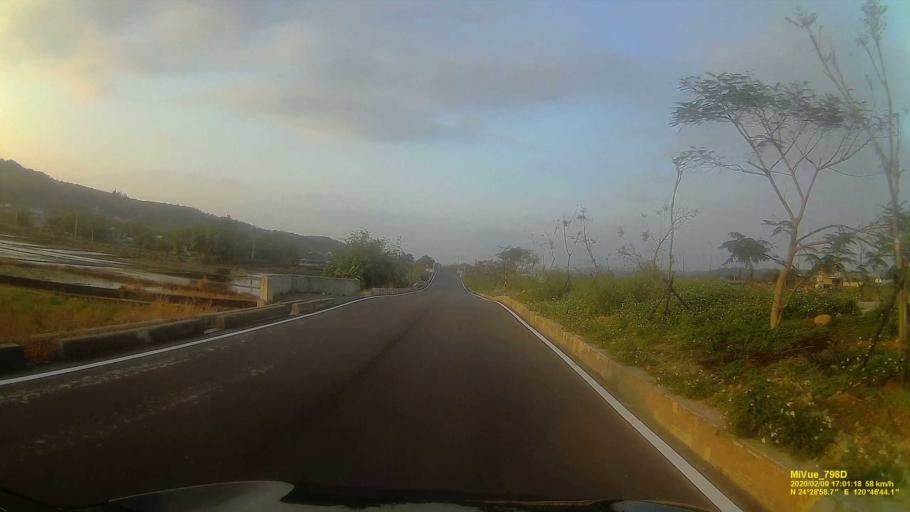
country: TW
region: Taiwan
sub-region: Miaoli
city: Miaoli
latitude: 24.4831
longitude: 120.7789
